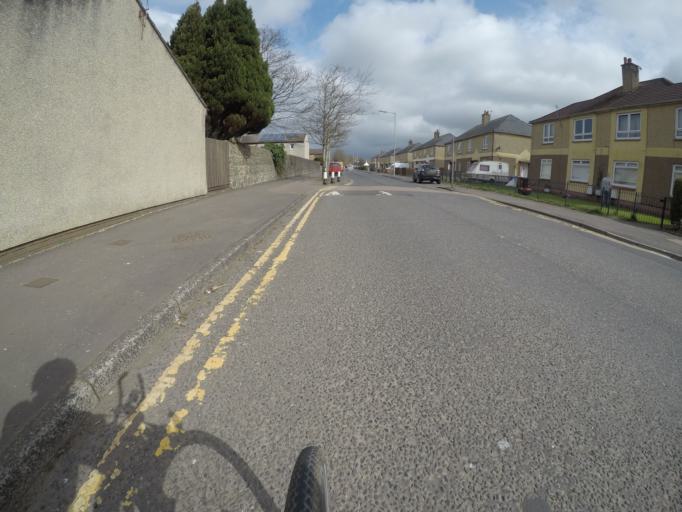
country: GB
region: Scotland
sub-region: North Ayrshire
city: Irvine
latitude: 55.6278
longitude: -4.6391
